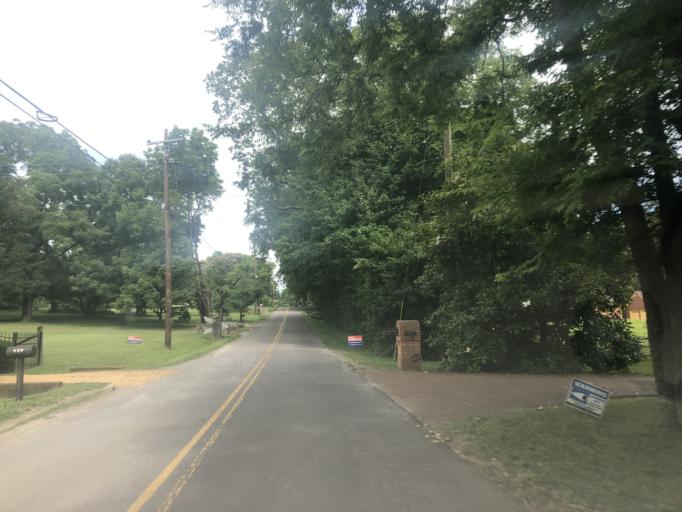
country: US
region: Tennessee
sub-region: Davidson County
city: Lakewood
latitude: 36.2188
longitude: -86.6595
